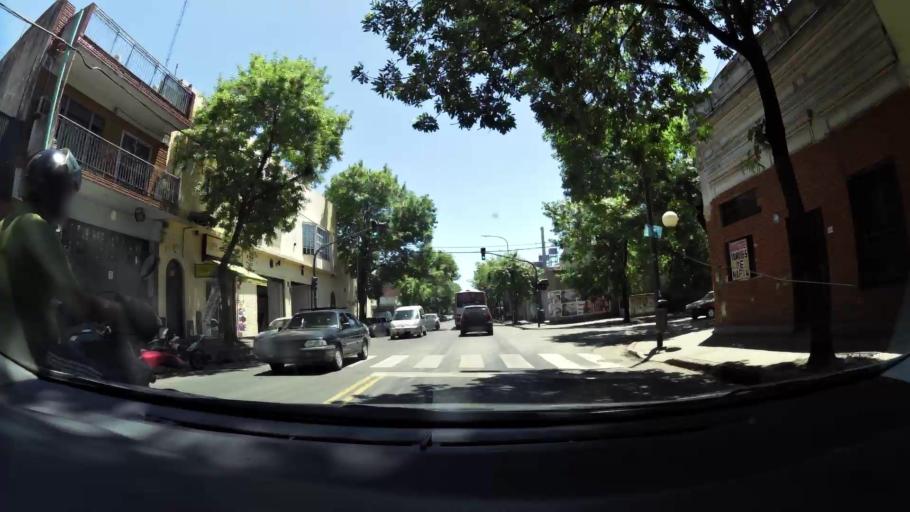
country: AR
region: Buenos Aires
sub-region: Partido de Avellaneda
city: Avellaneda
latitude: -34.6507
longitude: -58.3765
